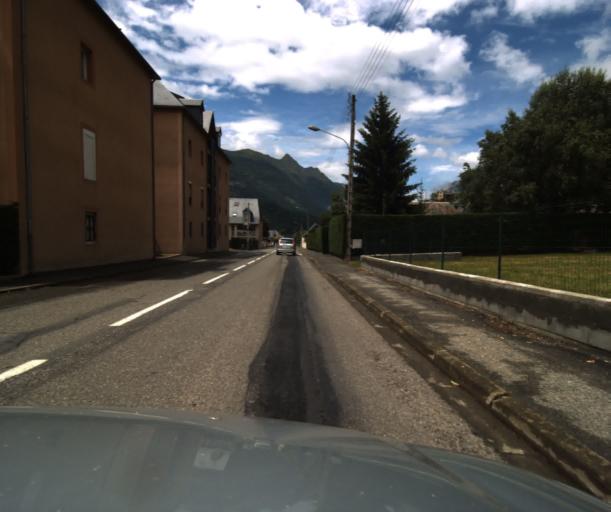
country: FR
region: Midi-Pyrenees
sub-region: Departement des Hautes-Pyrenees
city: Luz-Saint-Sauveur
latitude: 42.8768
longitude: -0.0066
